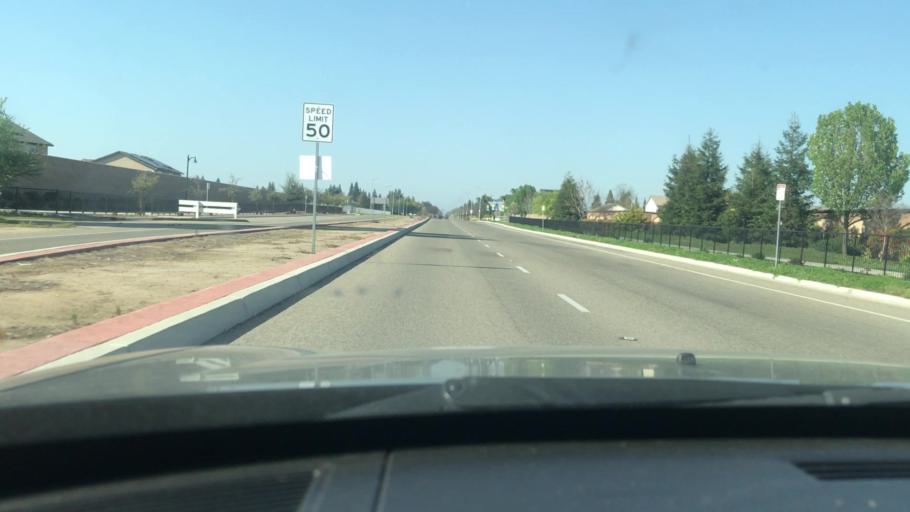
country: US
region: California
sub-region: Fresno County
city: Tarpey Village
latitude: 36.7875
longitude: -119.6639
